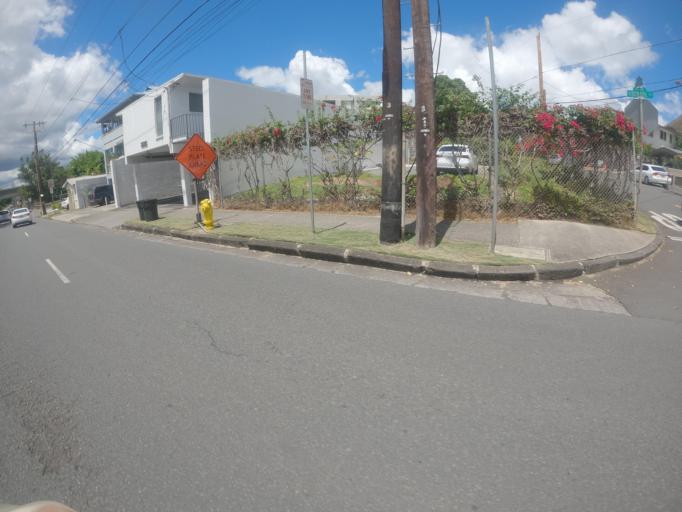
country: US
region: Hawaii
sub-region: Honolulu County
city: Honolulu
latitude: 21.3140
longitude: -157.8536
